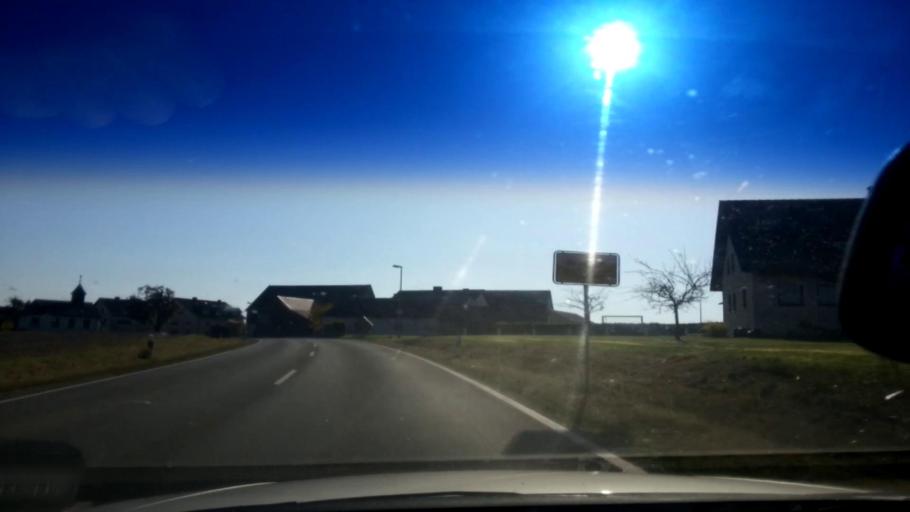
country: DE
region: Bavaria
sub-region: Upper Franconia
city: Stadelhofen
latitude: 49.9972
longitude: 11.2142
